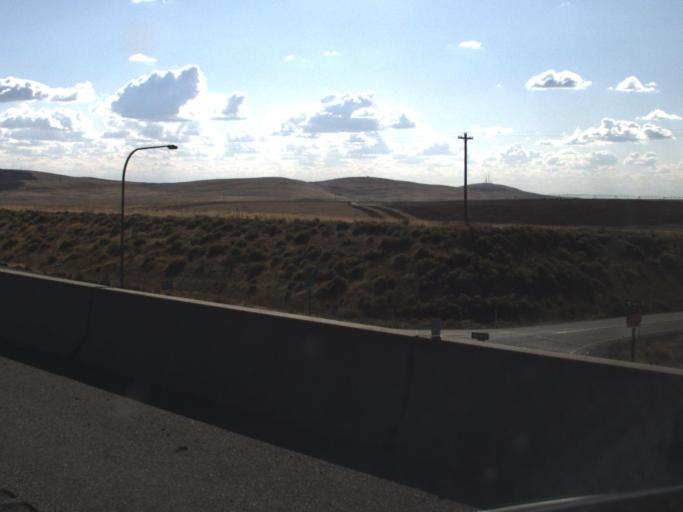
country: US
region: Washington
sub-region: Benton County
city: Highland
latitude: 46.0256
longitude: -119.2251
